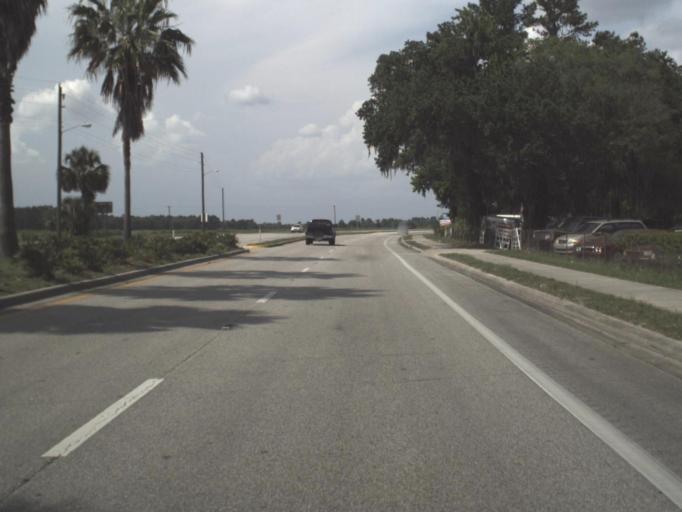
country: US
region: Florida
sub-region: Putnam County
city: East Palatka
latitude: 29.6622
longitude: -81.5937
